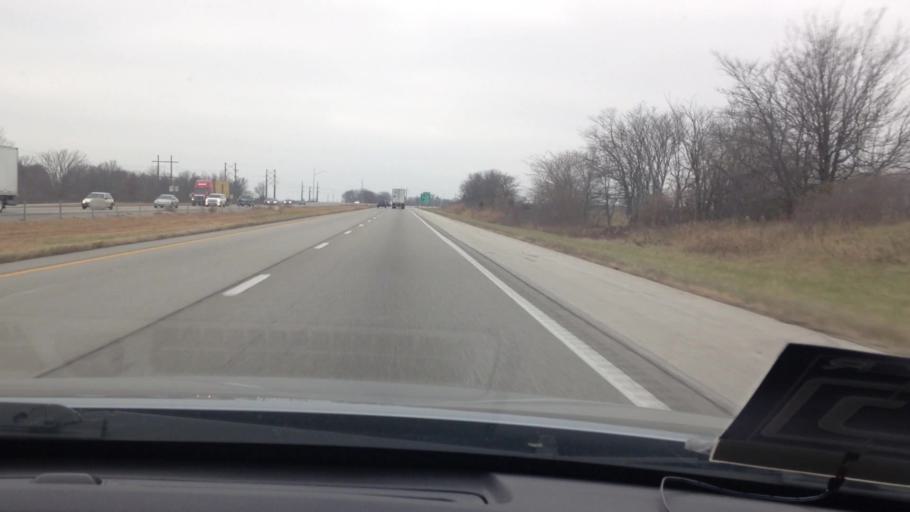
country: US
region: Missouri
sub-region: Cass County
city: Raymore
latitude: 38.7778
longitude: -94.4948
